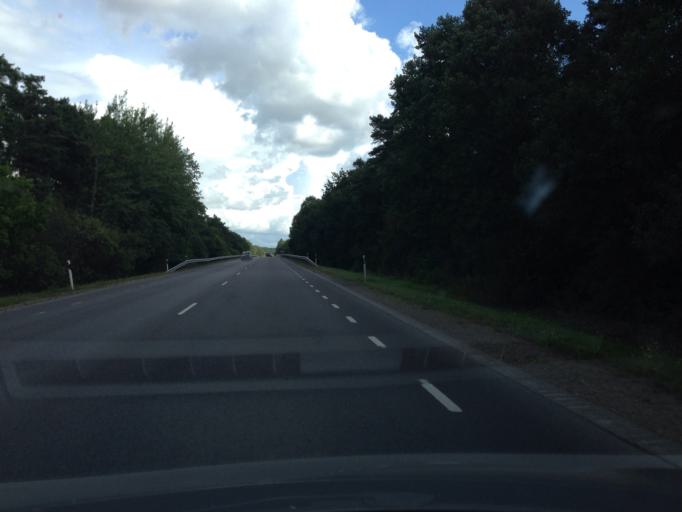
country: EE
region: Harju
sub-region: Saku vald
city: Saku
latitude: 59.3145
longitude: 24.6255
